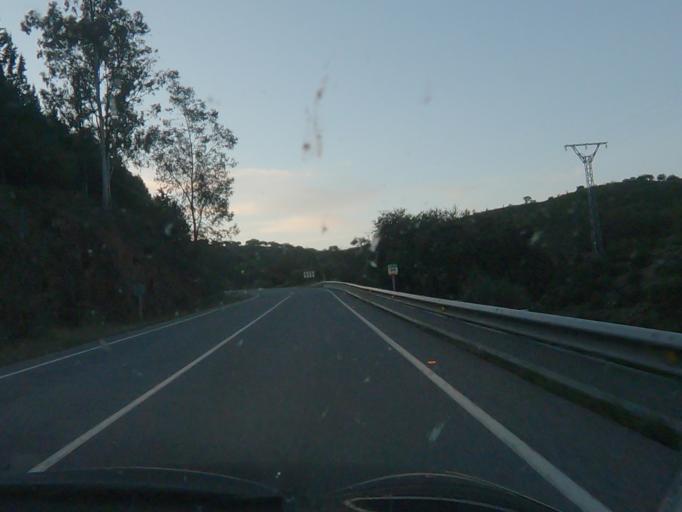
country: ES
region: Extremadura
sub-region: Provincia de Caceres
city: Alcantara
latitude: 39.7316
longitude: -6.8956
